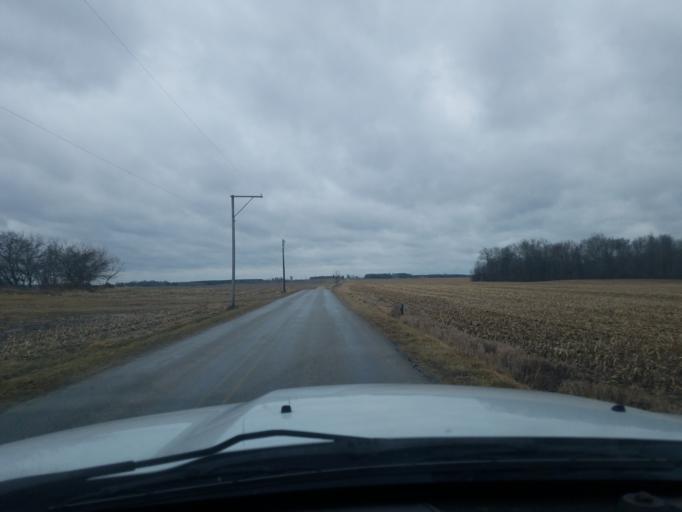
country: US
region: Indiana
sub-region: Noble County
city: Rome City
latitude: 41.4433
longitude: -85.3947
